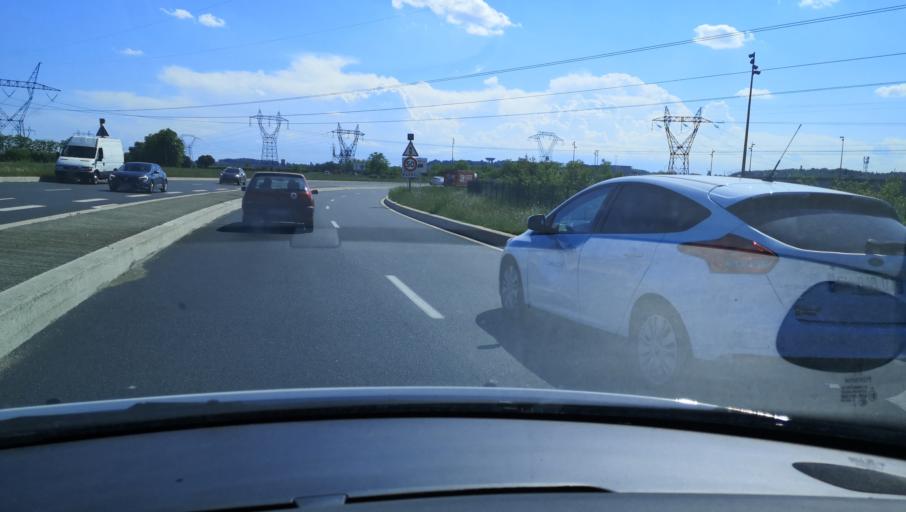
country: FR
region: Rhone-Alpes
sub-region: Departement du Rhone
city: Pusignan
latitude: 45.7623
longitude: 5.0355
